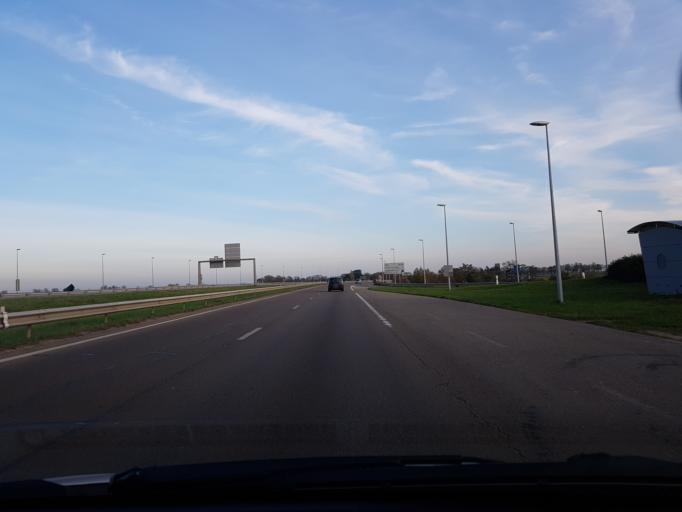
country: FR
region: Bourgogne
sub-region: Departement de la Cote-d'Or
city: Longvic
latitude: 47.3020
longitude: 5.0789
